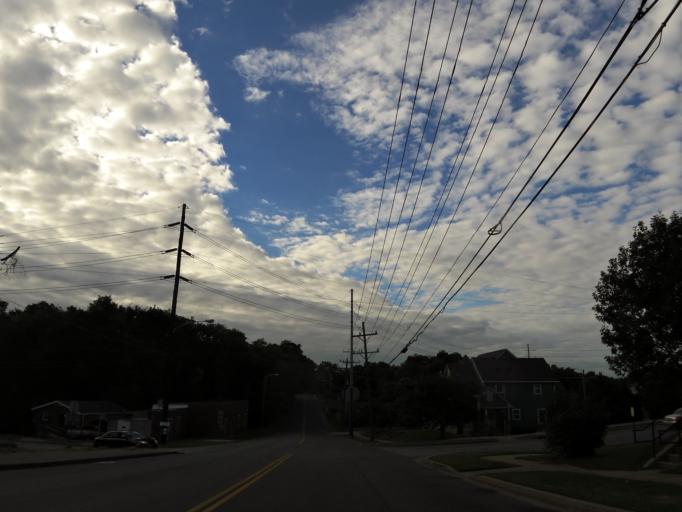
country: US
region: Tennessee
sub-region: Davidson County
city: Nashville
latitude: 36.1612
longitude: -86.8361
